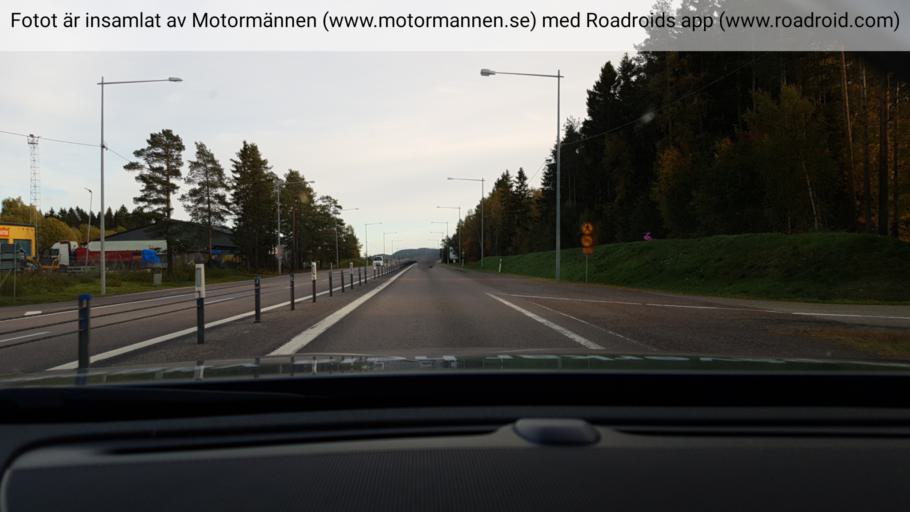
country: SE
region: Vaesternorrland
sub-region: Haernoesands Kommun
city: Haernoesand
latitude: 62.6491
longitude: 17.8952
